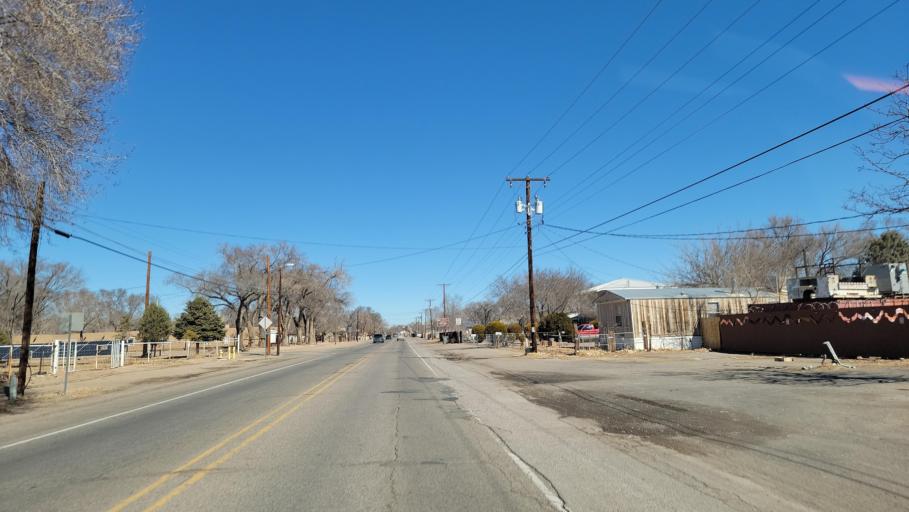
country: US
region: New Mexico
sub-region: Bernalillo County
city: South Valley
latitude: 34.9875
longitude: -106.6964
